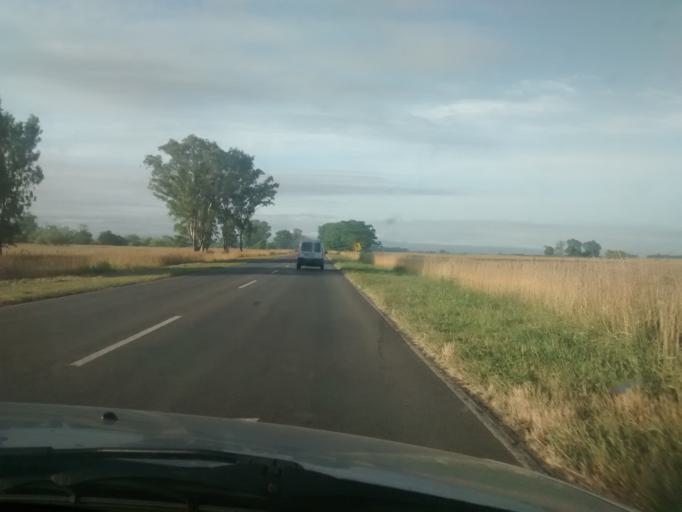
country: AR
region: Buenos Aires
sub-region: Partido de Brandsen
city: Brandsen
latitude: -35.2916
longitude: -58.2331
